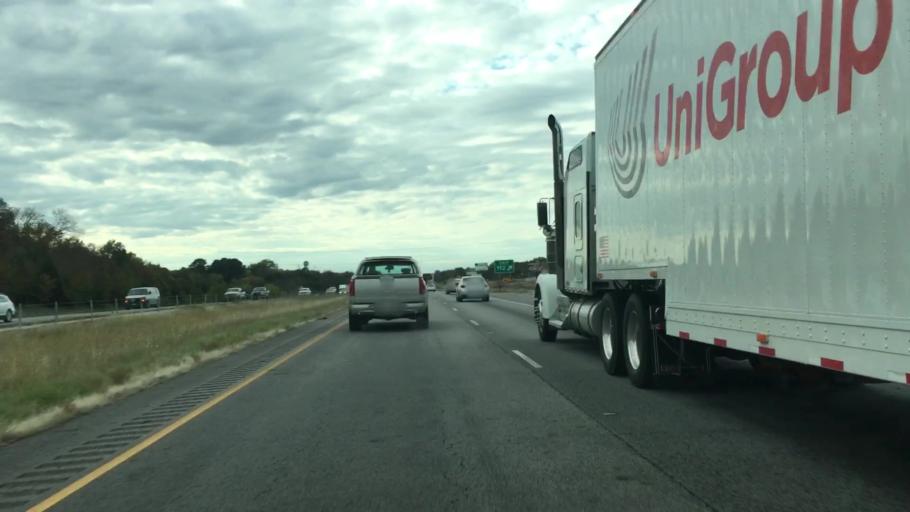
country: US
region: Arkansas
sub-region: Conway County
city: Morrilton
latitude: 35.1632
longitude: -92.6365
